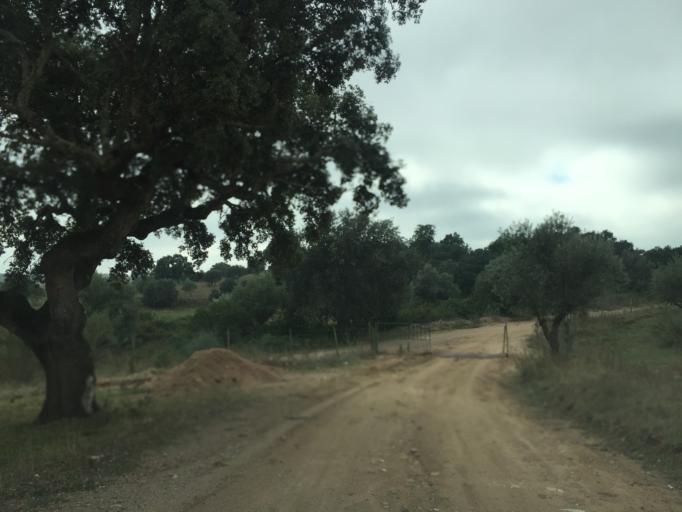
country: PT
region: Portalegre
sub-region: Fronteira
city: Fronteira
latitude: 39.0565
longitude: -7.6335
